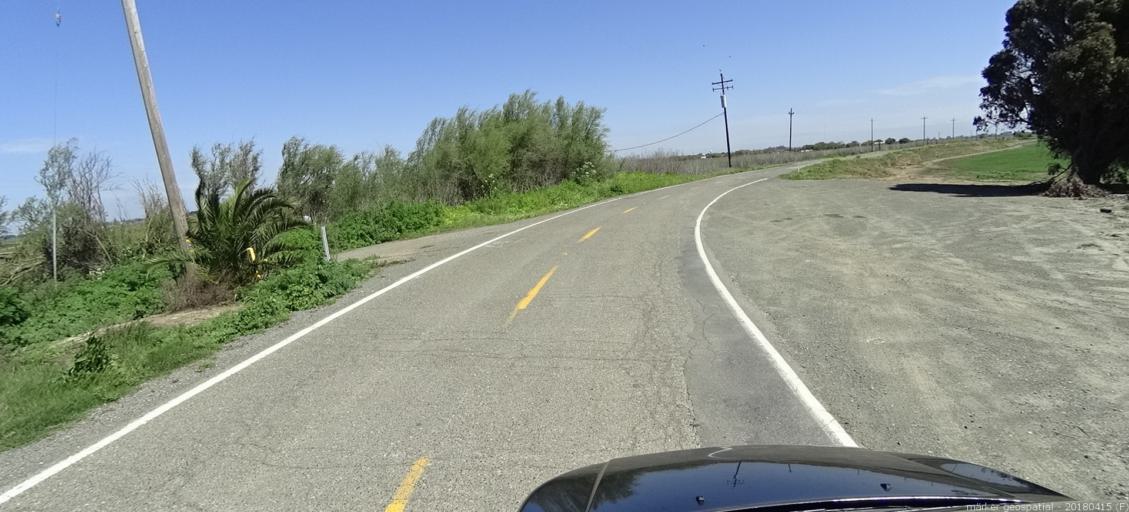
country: US
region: California
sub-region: Solano County
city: Rio Vista
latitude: 38.1431
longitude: -121.6243
